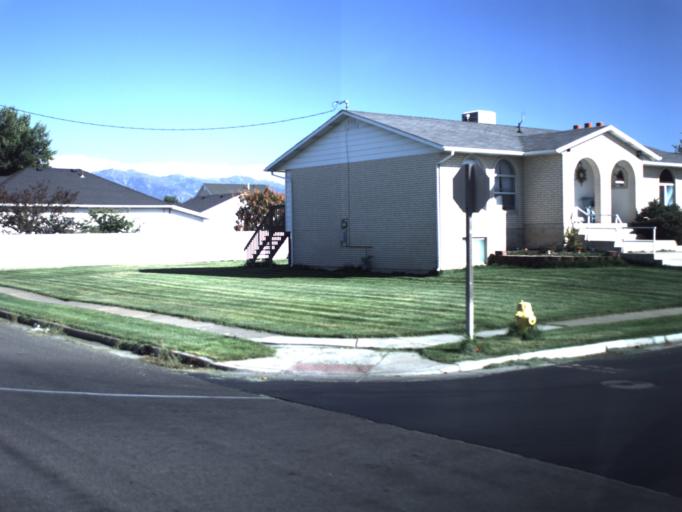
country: US
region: Utah
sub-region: Davis County
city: West Point
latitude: 41.1398
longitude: -112.0774
